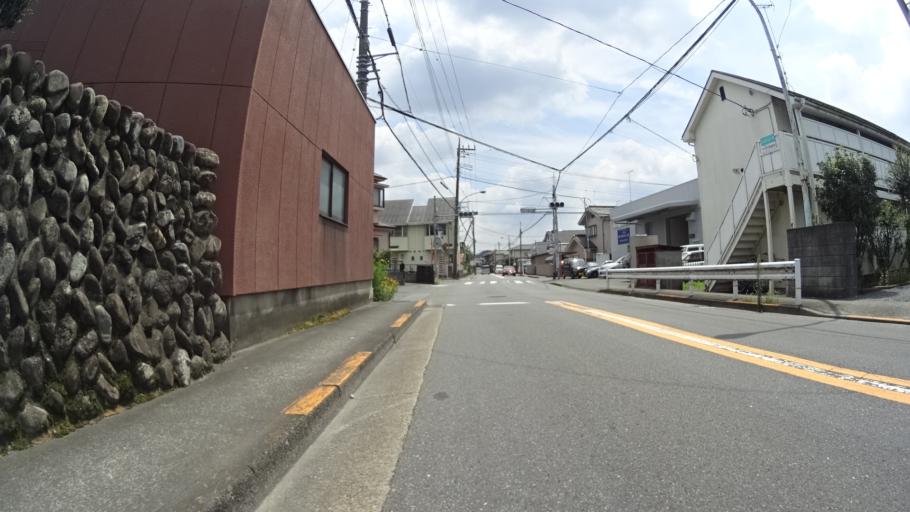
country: JP
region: Tokyo
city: Fussa
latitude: 35.7646
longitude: 139.3007
